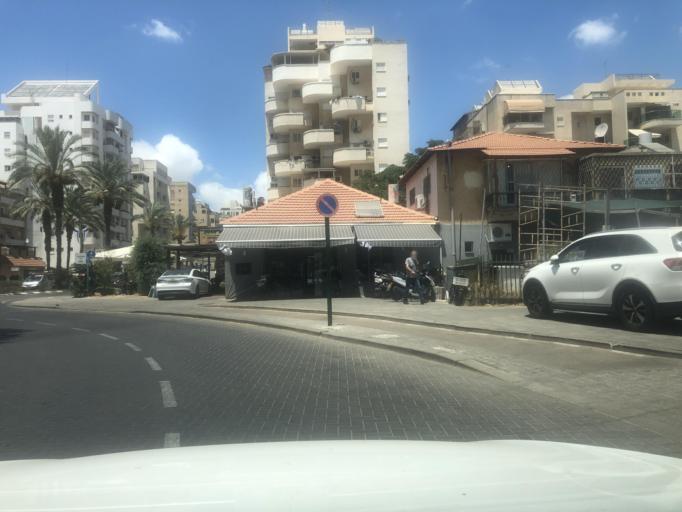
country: IL
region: Central District
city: Hod HaSharon
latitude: 32.1608
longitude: 34.9033
